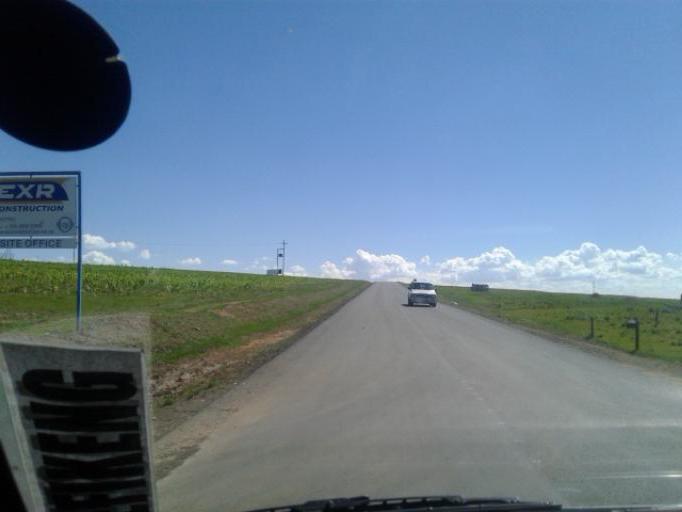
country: LS
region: Maseru
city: Maseru
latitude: -29.3070
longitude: 27.6048
